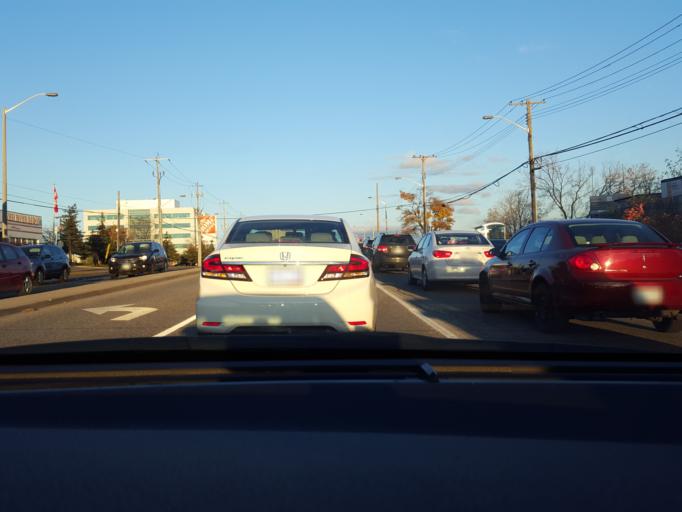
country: CA
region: Ontario
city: Scarborough
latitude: 43.7617
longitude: -79.2984
